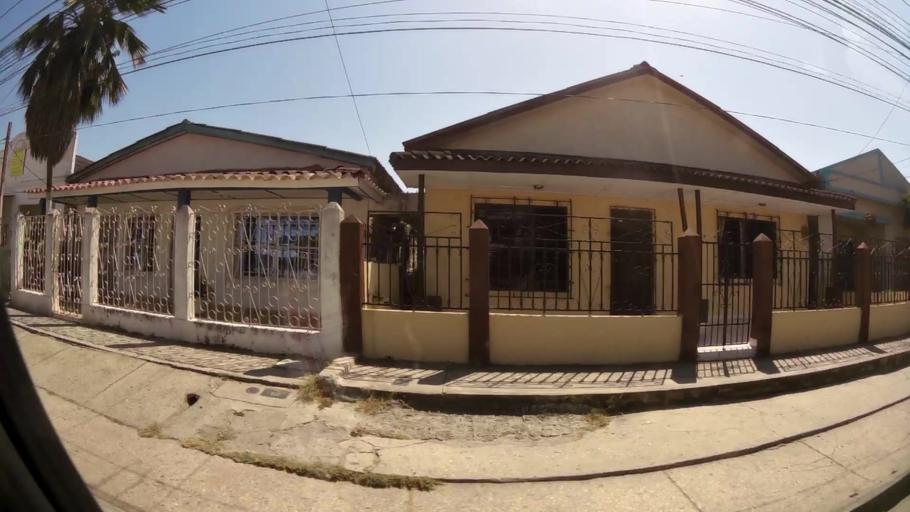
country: CO
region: Bolivar
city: Cartagena
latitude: 10.4375
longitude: -75.5221
